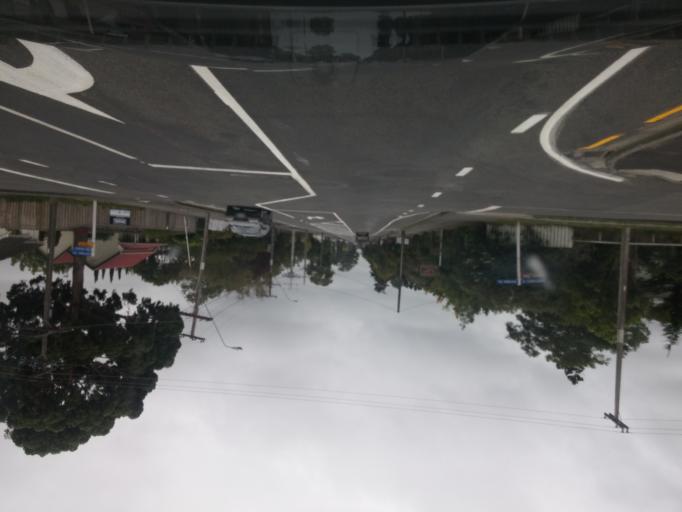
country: NZ
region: Wellington
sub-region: Masterton District
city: Masterton
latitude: -41.0871
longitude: 175.4529
